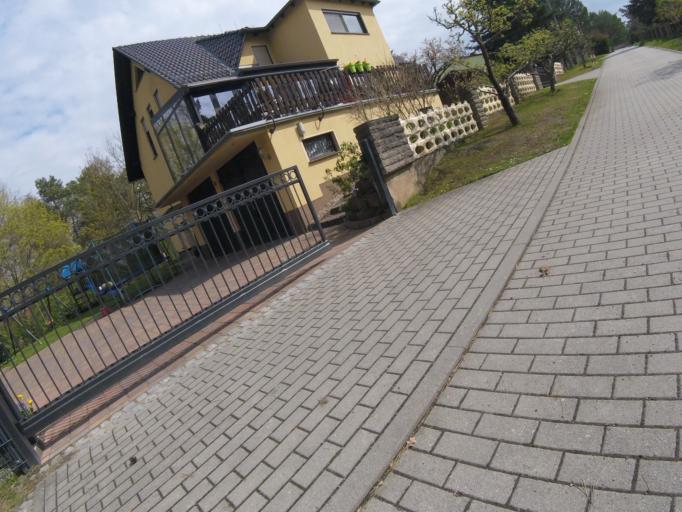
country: DE
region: Brandenburg
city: Gross Koris
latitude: 52.1632
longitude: 13.6505
